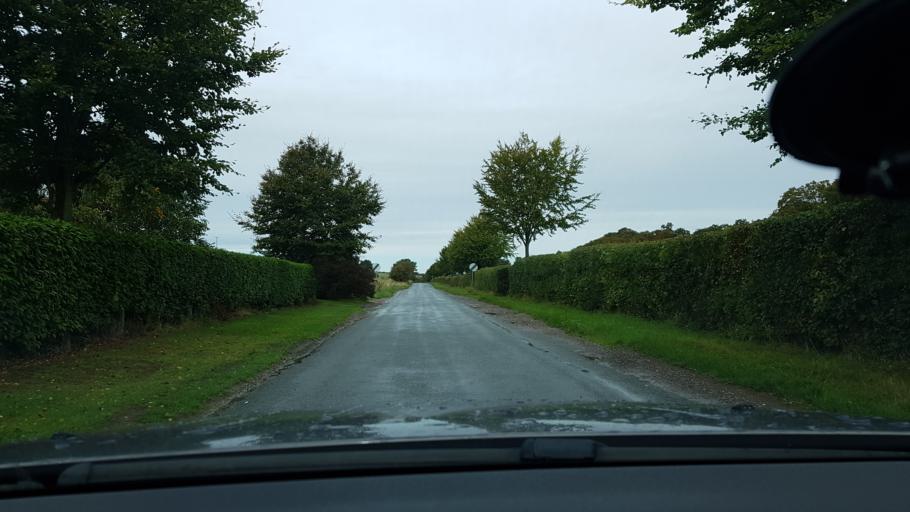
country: GB
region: England
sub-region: West Berkshire
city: Lambourn
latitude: 51.5291
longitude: -1.5249
